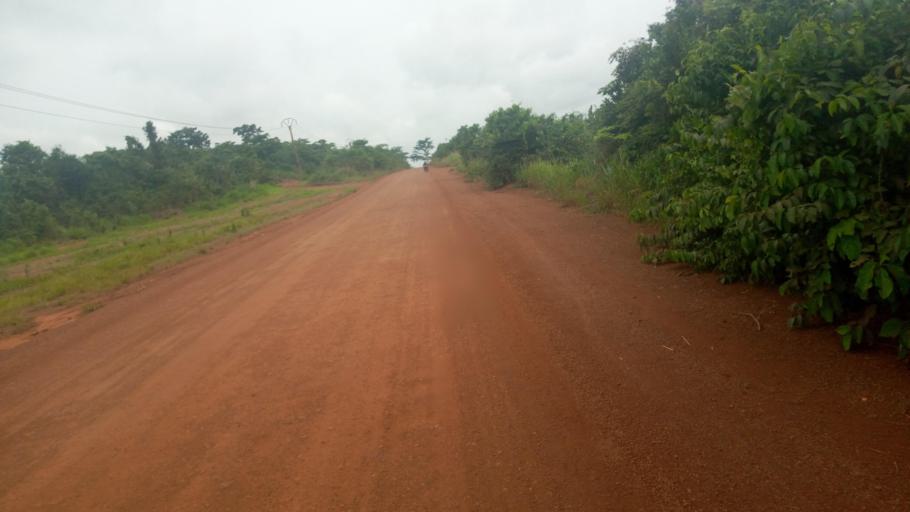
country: SL
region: Southern Province
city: Mogbwemo
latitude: 7.7392
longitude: -12.2838
